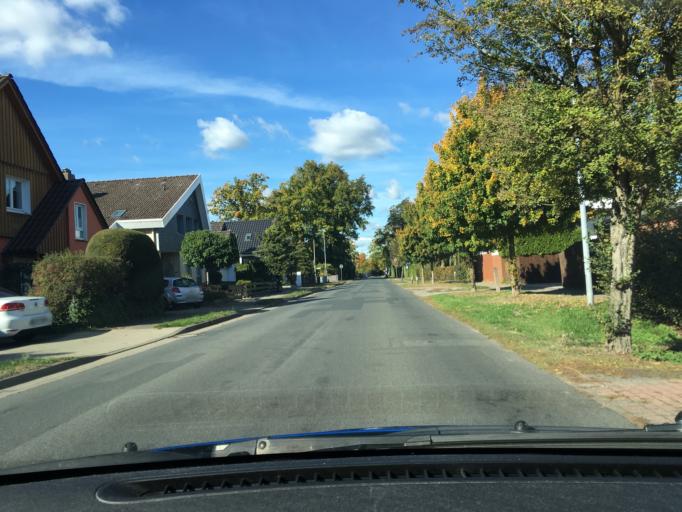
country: DE
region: Lower Saxony
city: Isernhagen Farster Bauerschaft
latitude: 52.4970
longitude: 9.8583
